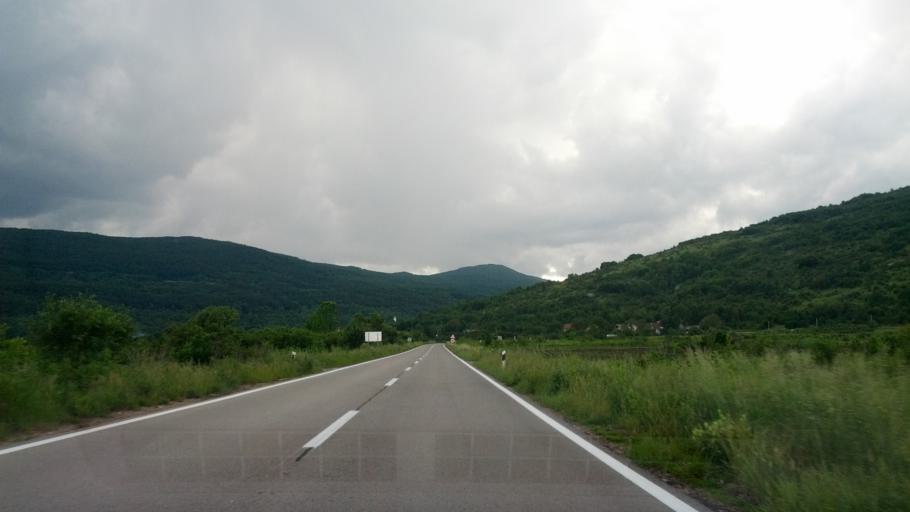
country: BA
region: Federation of Bosnia and Herzegovina
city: Izacic
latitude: 44.8795
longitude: 15.7321
